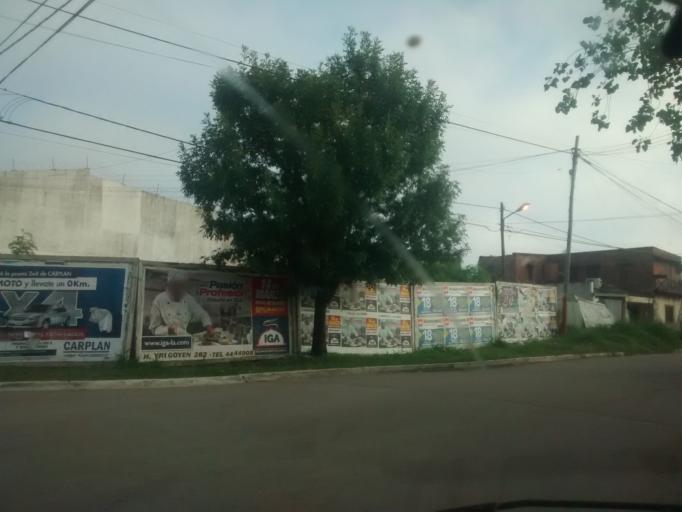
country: AR
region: Chaco
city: Resistencia
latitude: -27.4647
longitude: -58.9998
